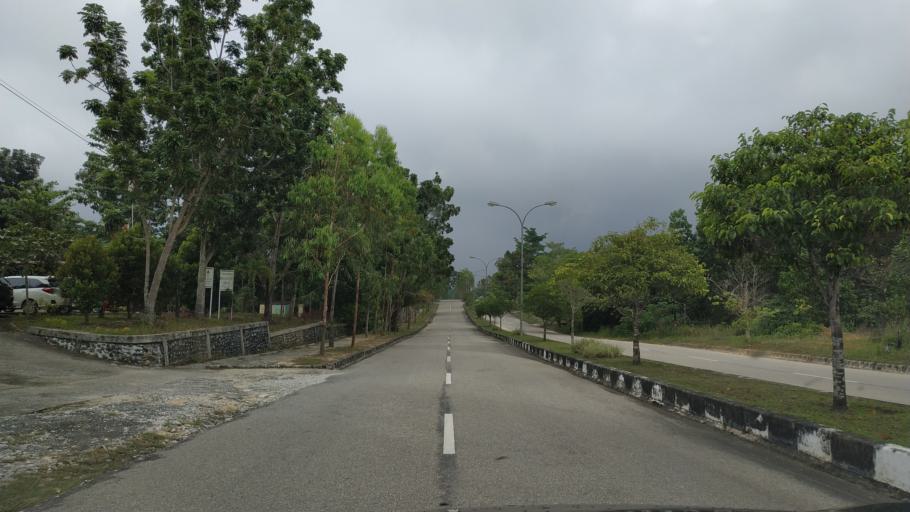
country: ID
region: Riau
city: Pangkalanbunut
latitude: 0.3827
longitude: 101.8289
